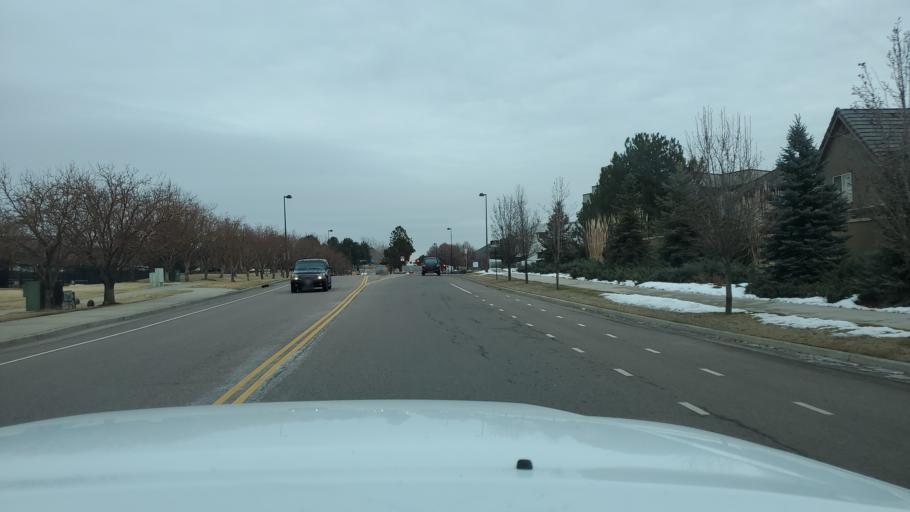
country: US
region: Colorado
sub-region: Arapahoe County
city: Castlewood
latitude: 39.6095
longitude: -104.9071
